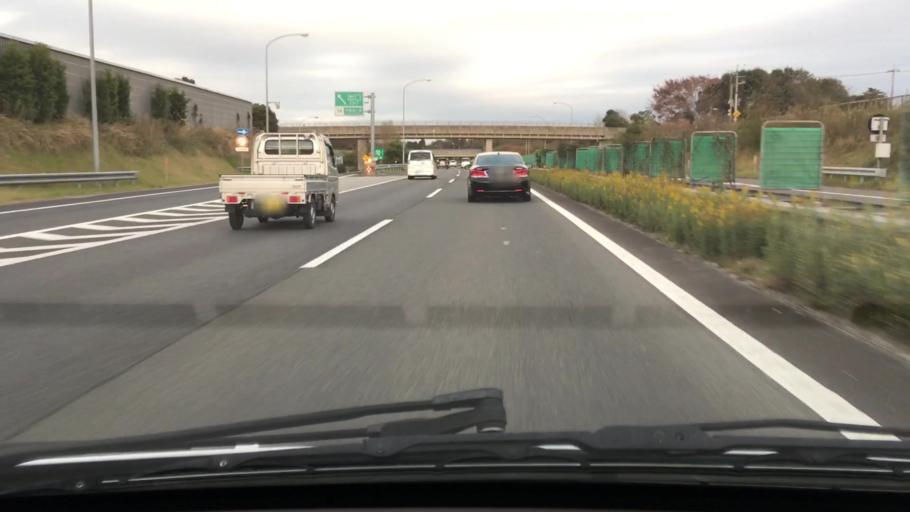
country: JP
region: Chiba
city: Ichihara
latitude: 35.4267
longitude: 140.0402
